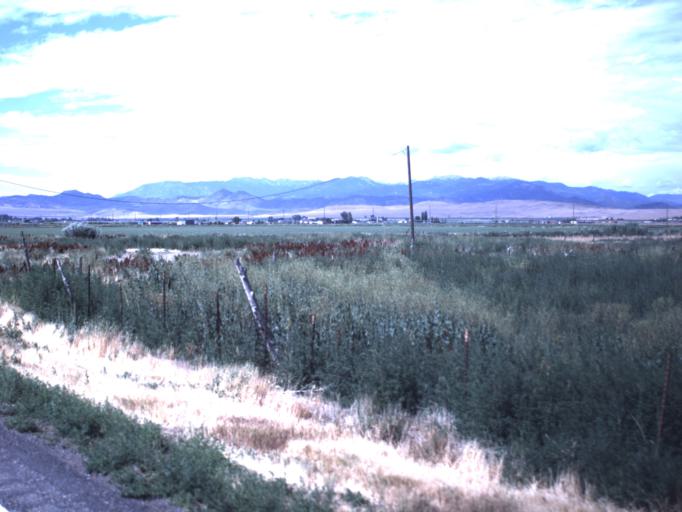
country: US
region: Utah
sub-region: Sevier County
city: Monroe
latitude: 38.6672
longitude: -112.1209
